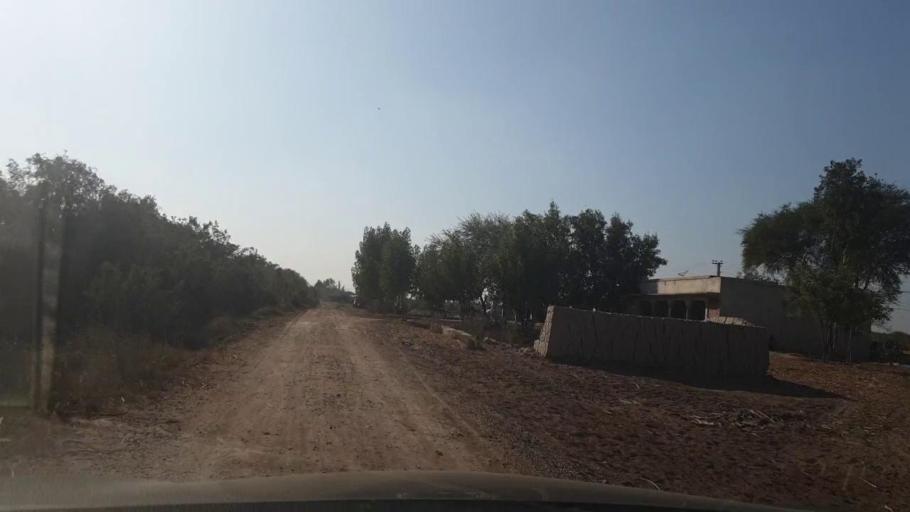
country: PK
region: Sindh
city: Khairpur
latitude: 28.1360
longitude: 69.6014
